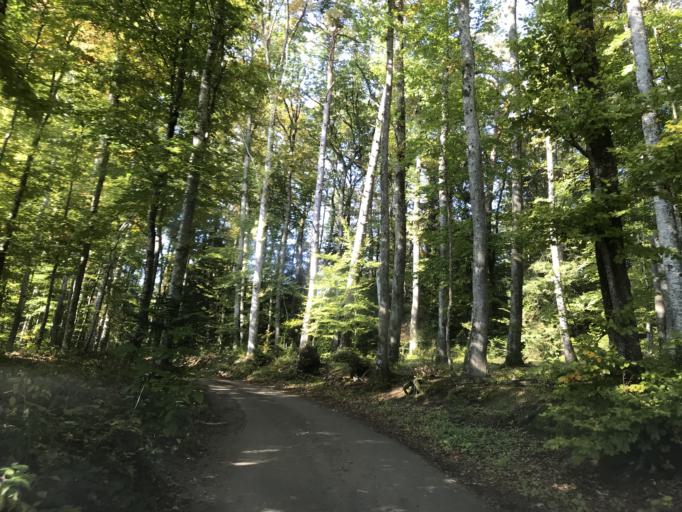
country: DE
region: Baden-Wuerttemberg
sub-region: Freiburg Region
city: Gorwihl
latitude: 47.6354
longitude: 8.0616
